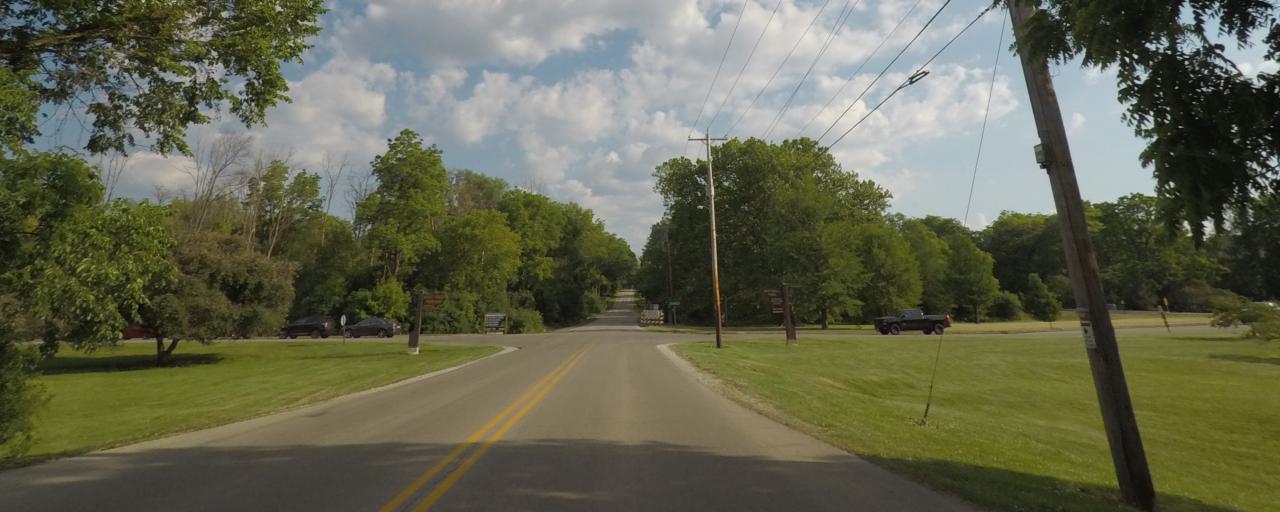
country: US
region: Wisconsin
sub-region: Milwaukee County
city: Hales Corners
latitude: 42.9309
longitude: -88.0286
